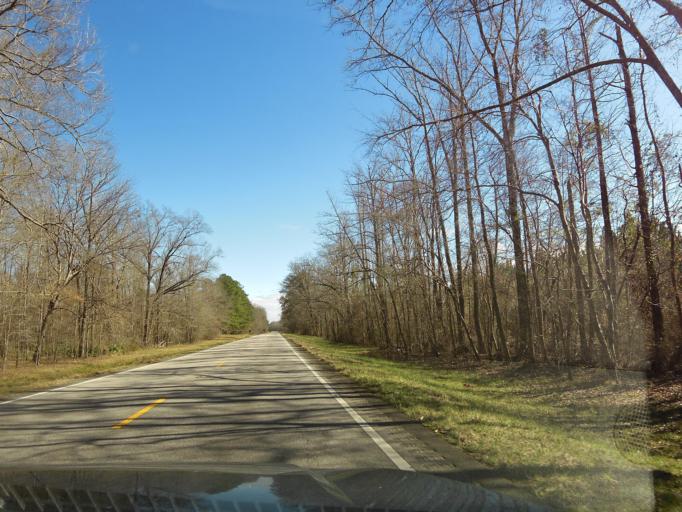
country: US
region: Alabama
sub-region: Barbour County
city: Clayton
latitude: 32.0486
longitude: -85.4350
